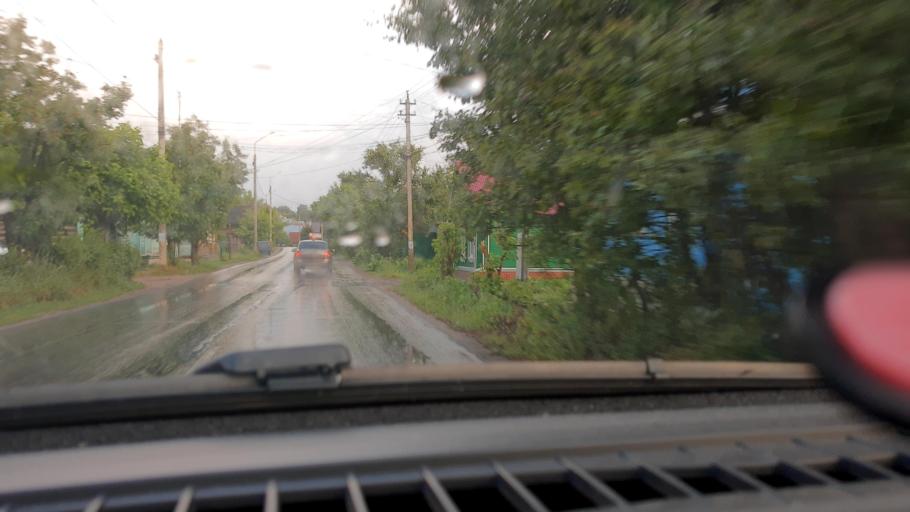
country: RU
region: Nizjnij Novgorod
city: Gorodets
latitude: 56.6589
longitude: 43.4625
